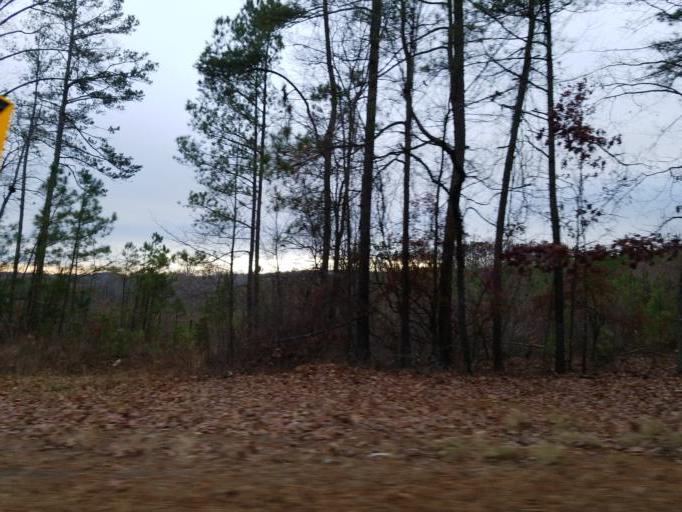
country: US
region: Georgia
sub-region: Dawson County
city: Dawsonville
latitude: 34.4325
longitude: -84.0761
